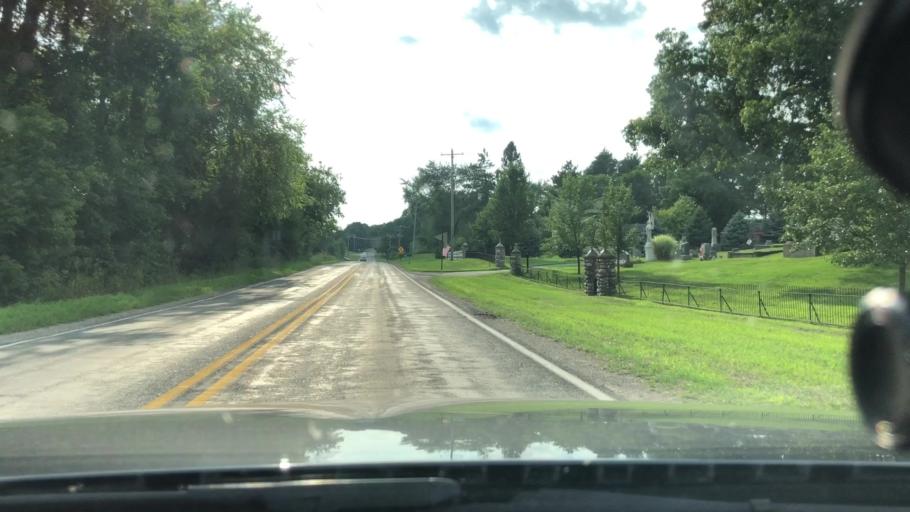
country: US
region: Michigan
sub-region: Washtenaw County
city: Manchester
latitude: 42.1446
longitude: -84.0563
